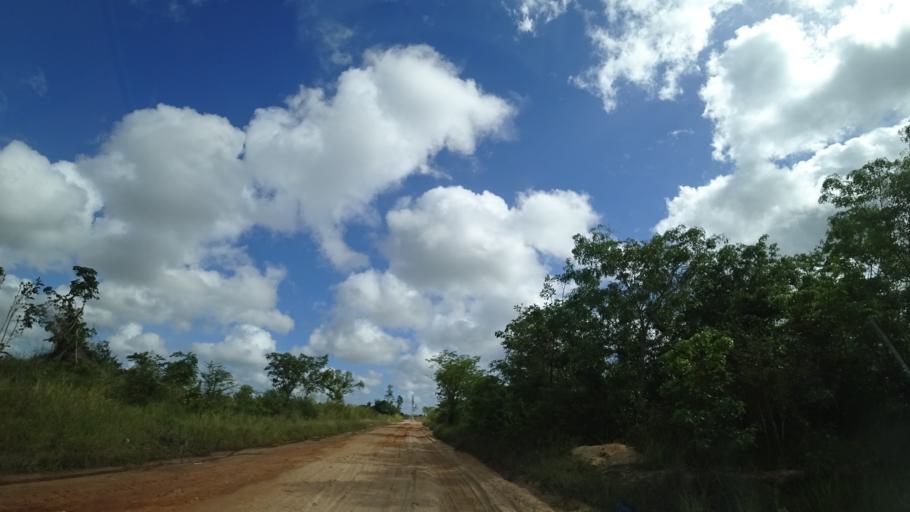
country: MZ
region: Sofala
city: Dondo
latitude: -19.4316
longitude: 34.7103
